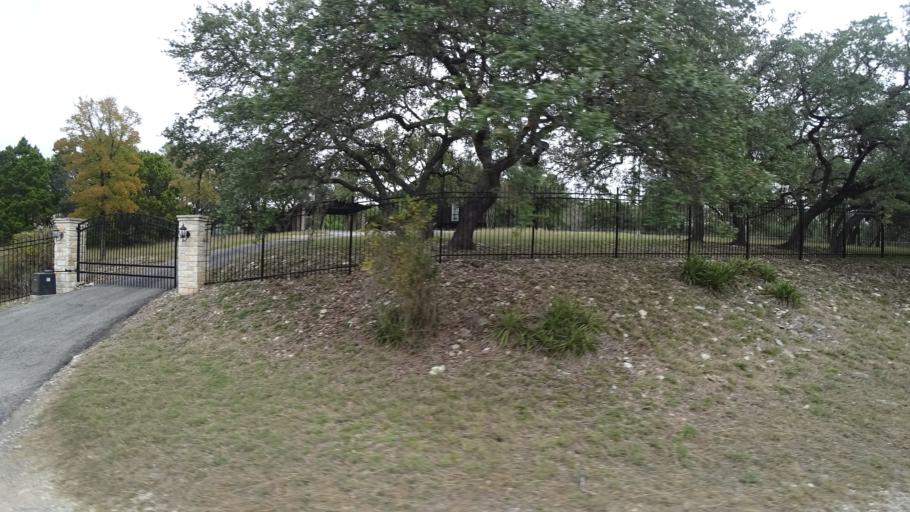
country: US
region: Texas
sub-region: Williamson County
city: Anderson Mill
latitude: 30.4502
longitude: -97.8378
